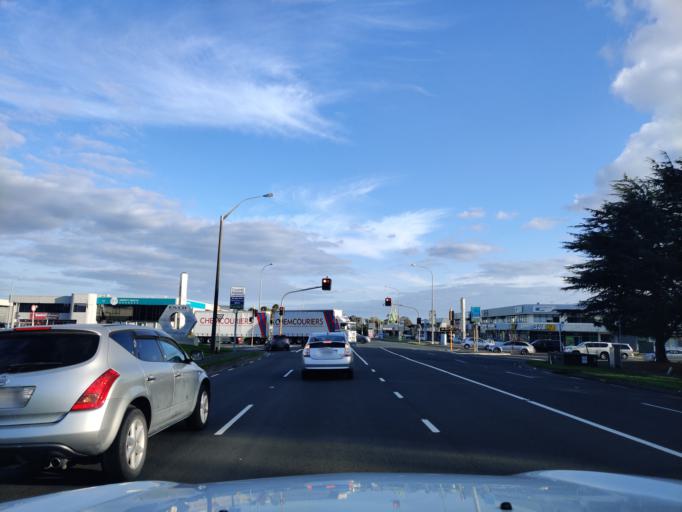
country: NZ
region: Auckland
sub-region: Auckland
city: Manukau City
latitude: -36.9482
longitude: 174.8925
